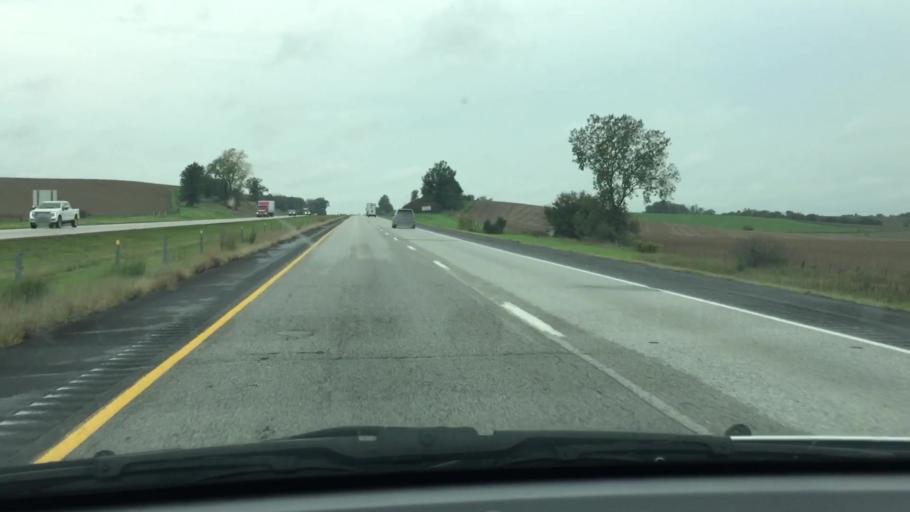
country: US
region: Iowa
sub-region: Johnson County
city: Tiffin
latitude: 41.6952
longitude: -91.7034
